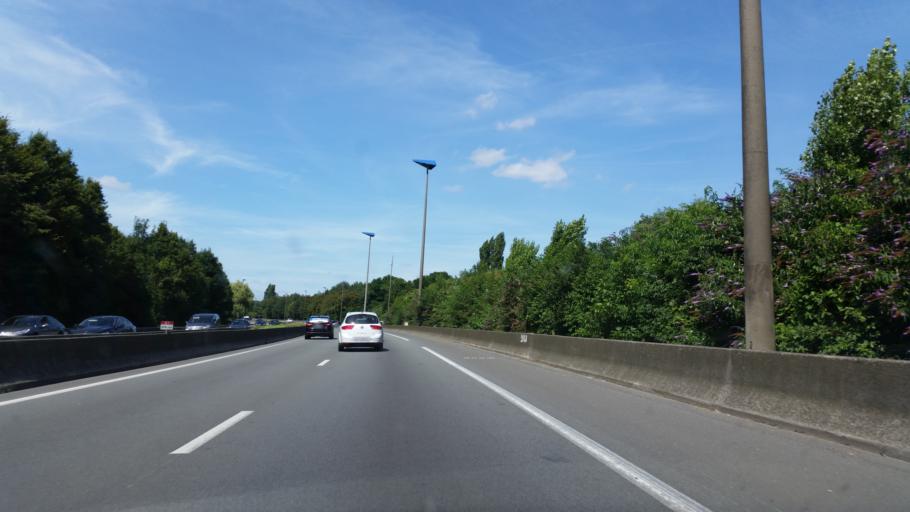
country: FR
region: Nord-Pas-de-Calais
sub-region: Departement du Nord
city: Ronchin
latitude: 50.6018
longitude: 3.1029
